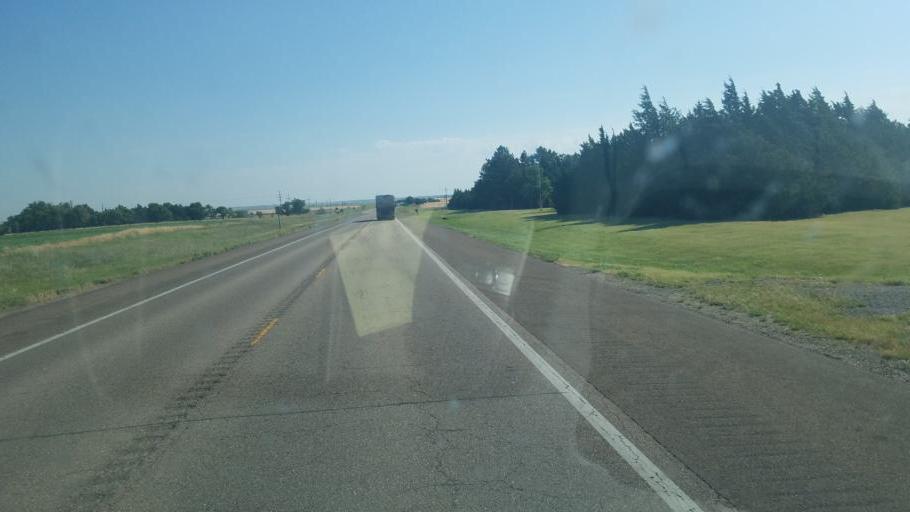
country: US
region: Kansas
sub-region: Barton County
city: Ellinwood
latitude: 38.4021
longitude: -98.6680
